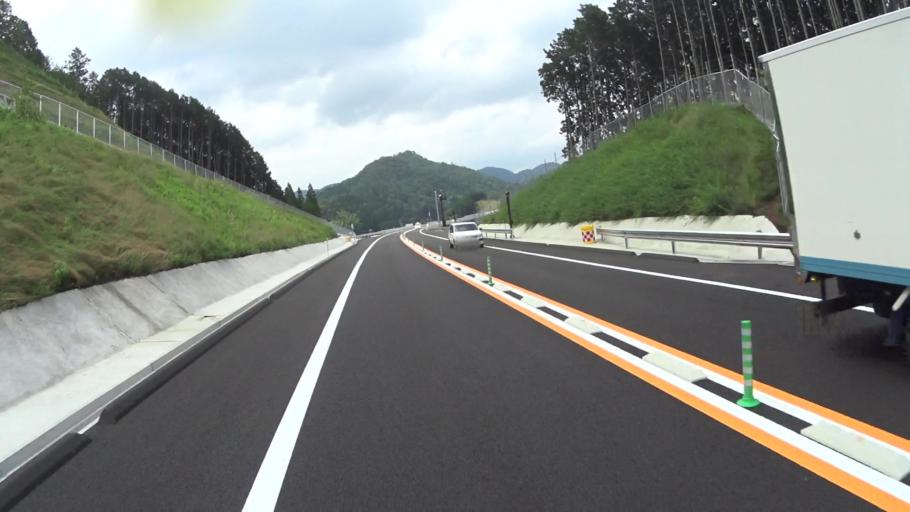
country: JP
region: Kyoto
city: Ayabe
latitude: 35.2146
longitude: 135.3434
